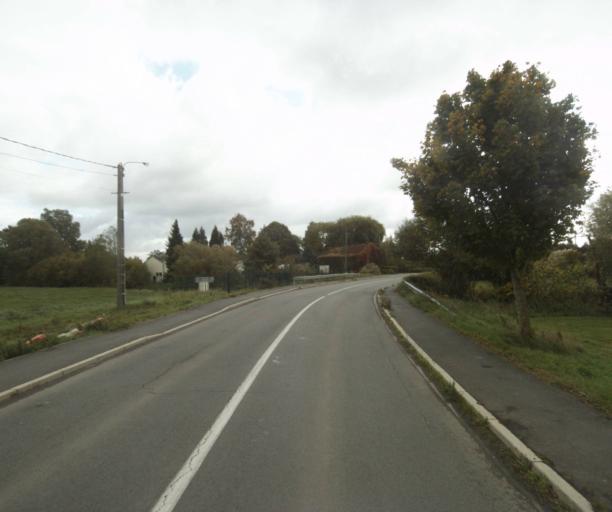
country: FR
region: Nord-Pas-de-Calais
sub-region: Departement du Nord
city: Verlinghem
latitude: 50.6974
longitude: 3.0184
